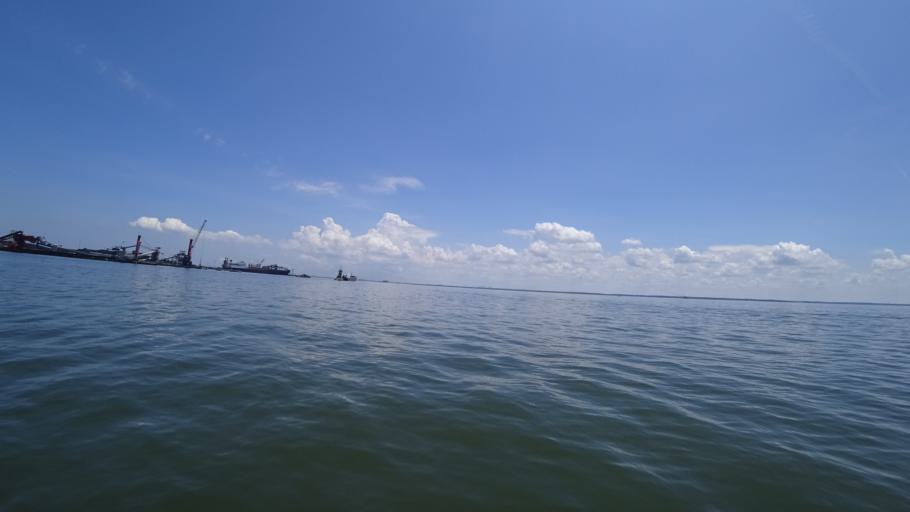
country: US
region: Virginia
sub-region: City of Newport News
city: Newport News
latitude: 36.9669
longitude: -76.4366
